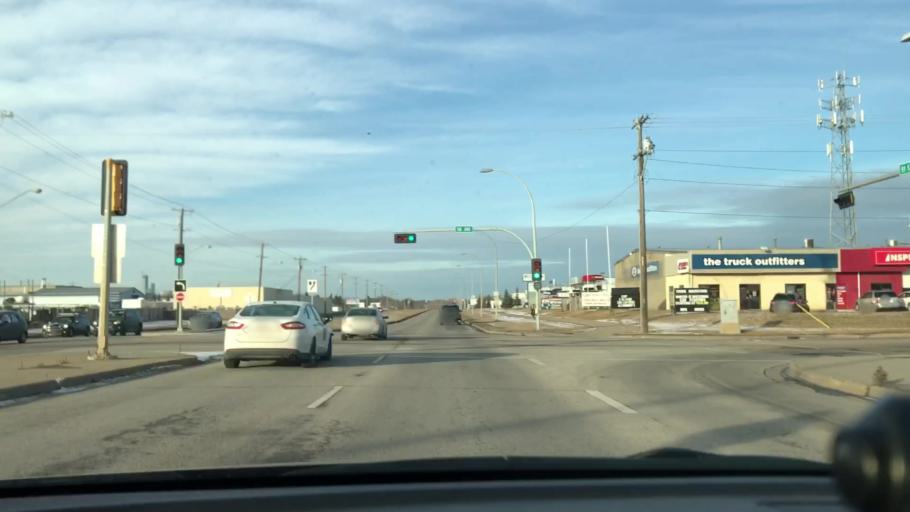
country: CA
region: Alberta
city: Edmonton
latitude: 53.4937
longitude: -113.4670
